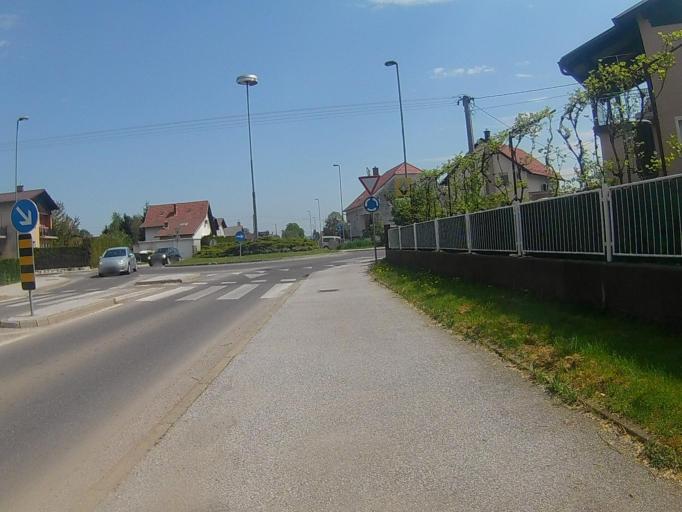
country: SI
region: Maribor
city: Kamnica
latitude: 46.5552
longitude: 15.6149
